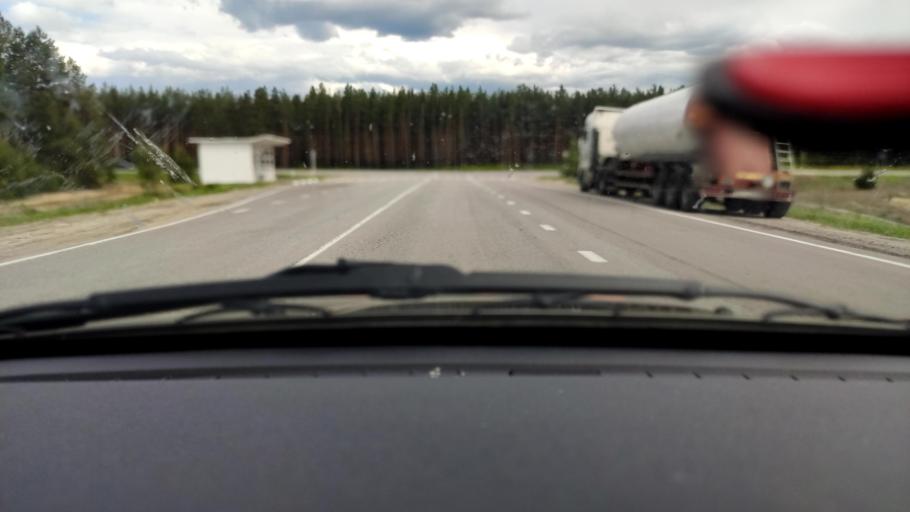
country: RU
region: Voronezj
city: Uryv-Pokrovka
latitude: 51.0495
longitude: 38.9821
